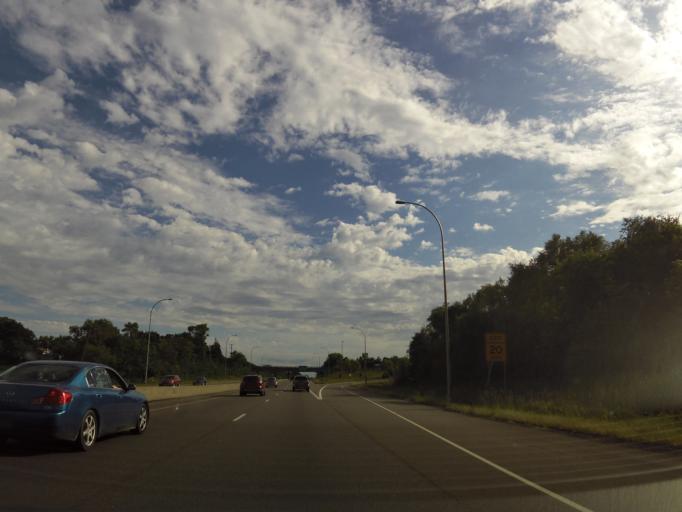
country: US
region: Minnesota
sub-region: Hennepin County
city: New Hope
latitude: 45.0720
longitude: -93.4015
